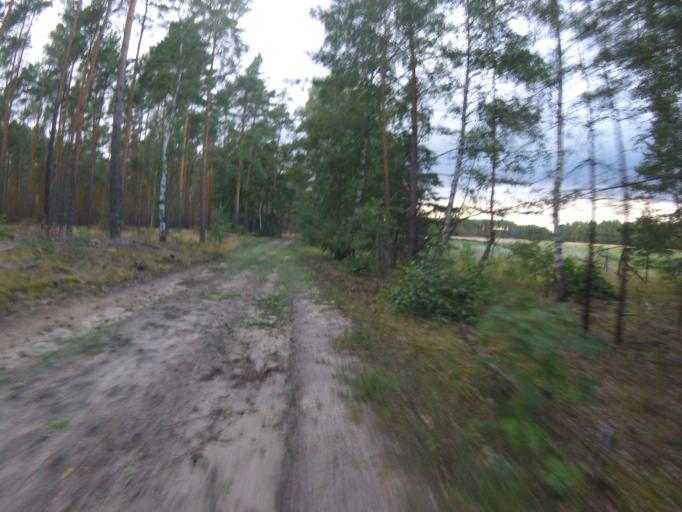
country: DE
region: Brandenburg
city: Bestensee
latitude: 52.2117
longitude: 13.6724
